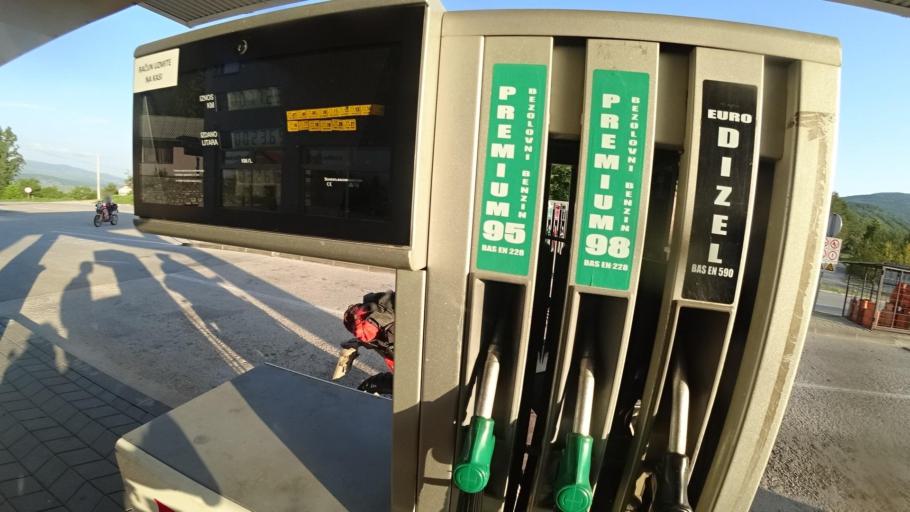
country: BA
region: Federation of Bosnia and Herzegovina
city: Bosansko Grahovo
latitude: 44.1821
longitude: 16.3675
